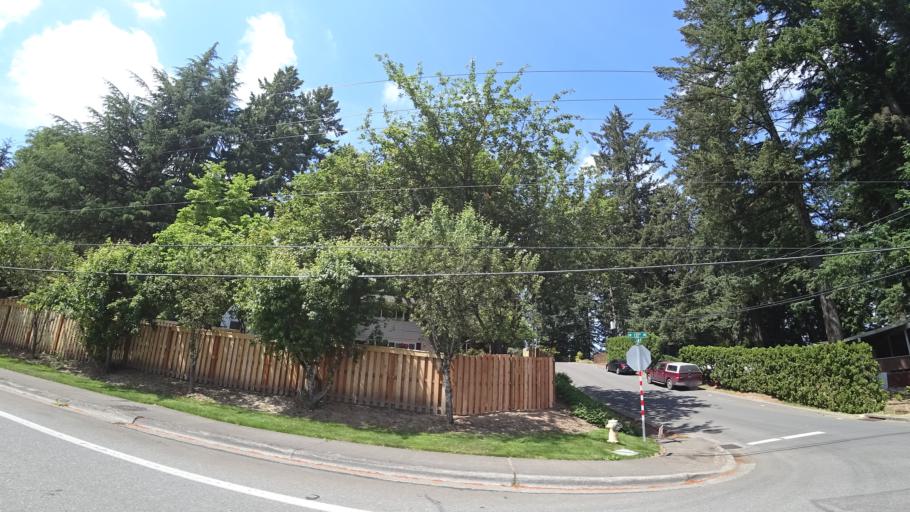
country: US
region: Oregon
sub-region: Washington County
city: King City
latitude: 45.4275
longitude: -122.8158
